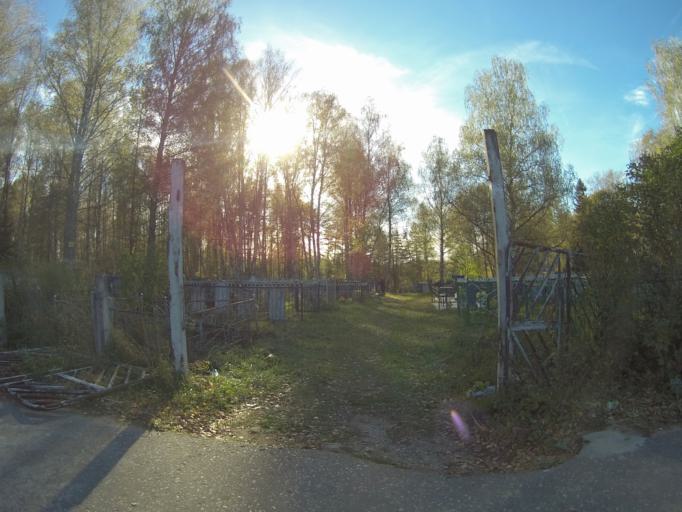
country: RU
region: Vladimir
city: Golovino
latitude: 55.9842
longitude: 40.5226
